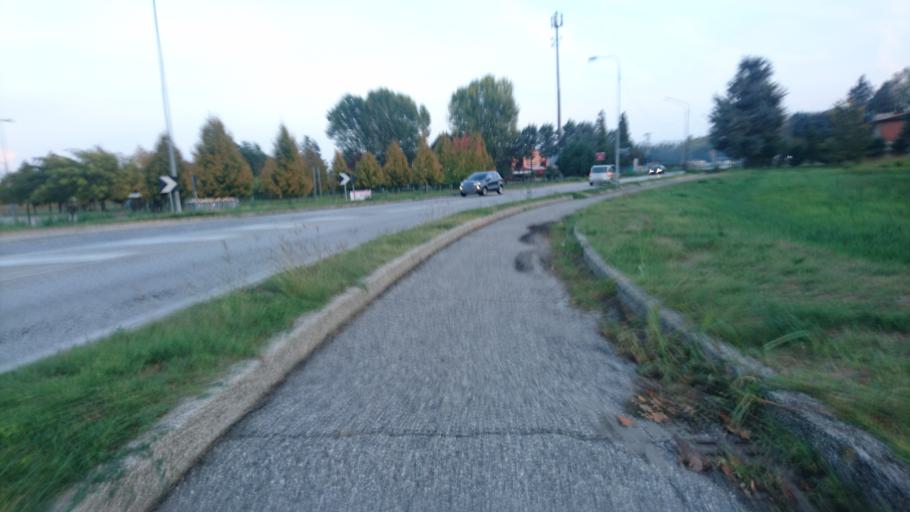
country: IT
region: Emilia-Romagna
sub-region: Provincia di Ferrara
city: Ferrara
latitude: 44.8592
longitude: 11.6130
